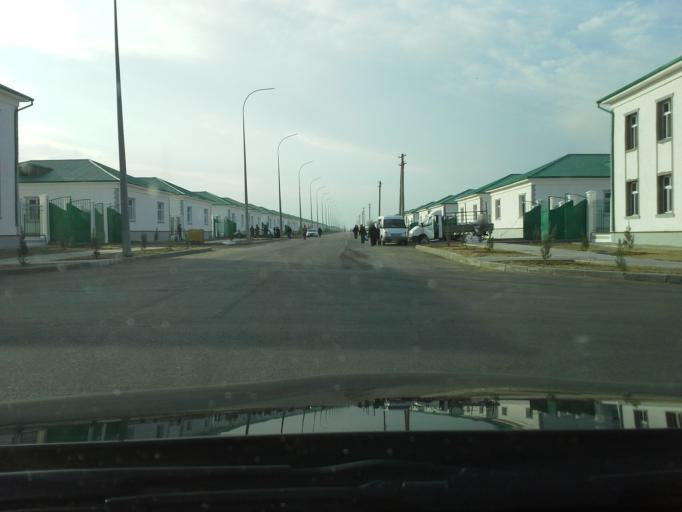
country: TM
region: Ahal
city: Abadan
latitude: 38.0969
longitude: 58.3195
